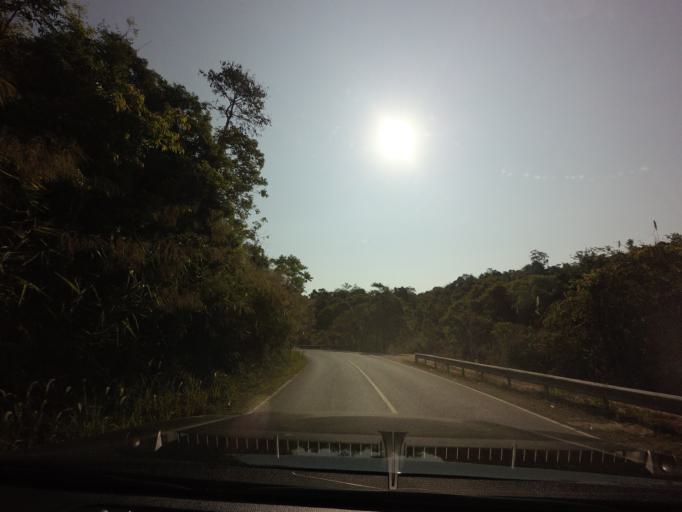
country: TH
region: Kanchanaburi
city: Thong Pha Phum
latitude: 14.6760
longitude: 98.3726
